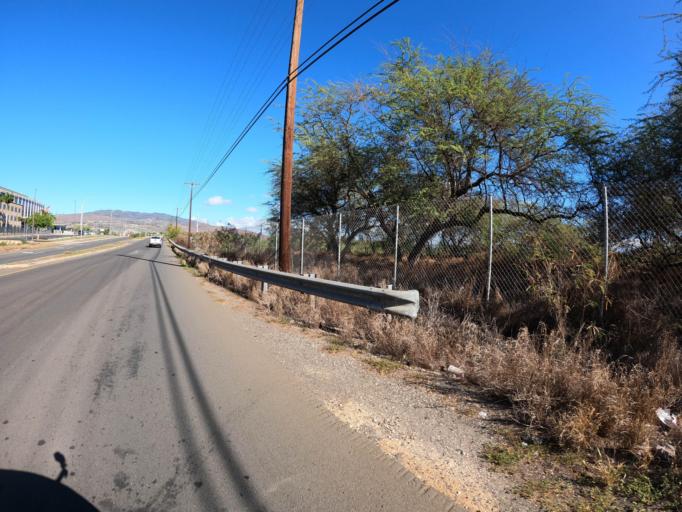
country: US
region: Hawaii
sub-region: Honolulu County
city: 'Ewa Villages
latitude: 21.3225
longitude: -158.0666
